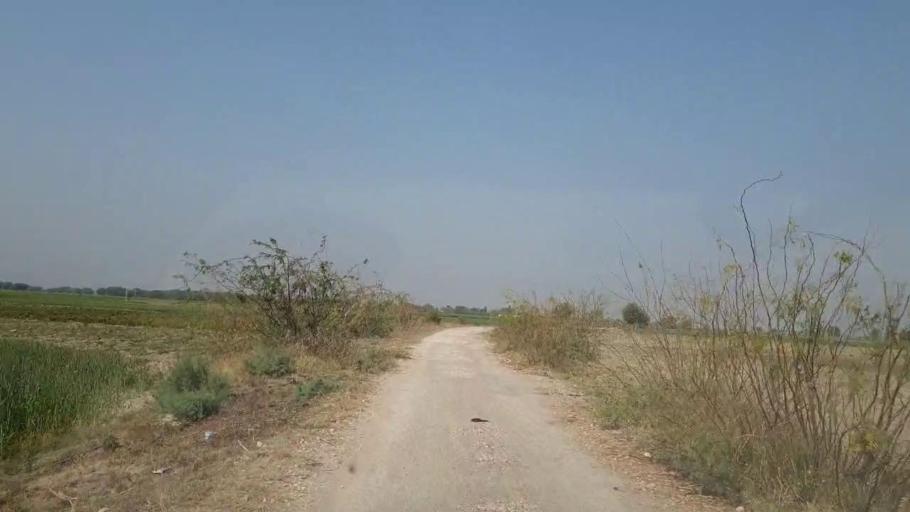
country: PK
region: Sindh
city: Mirpur Khas
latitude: 25.6420
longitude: 69.1306
